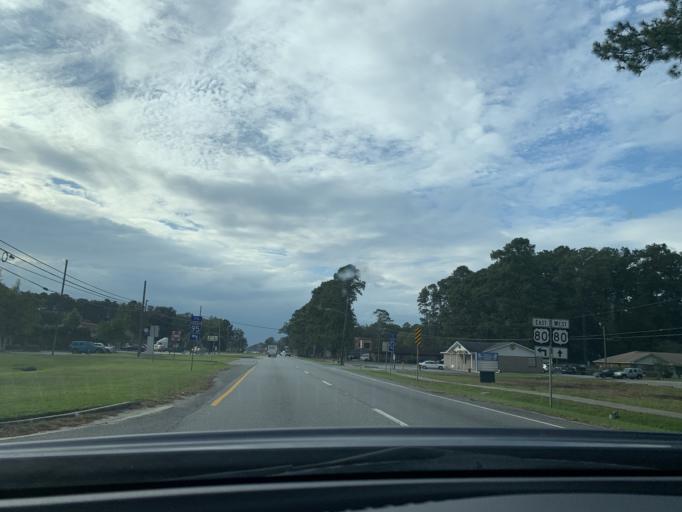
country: US
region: Georgia
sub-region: Chatham County
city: Pooler
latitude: 32.1181
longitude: -81.2545
